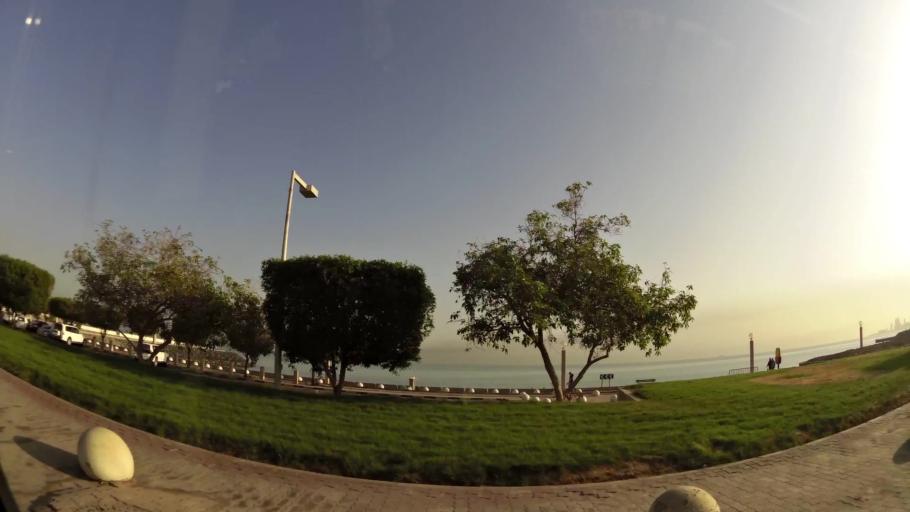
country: KW
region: Muhafazat Hawalli
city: Hawalli
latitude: 29.3484
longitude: 48.0370
